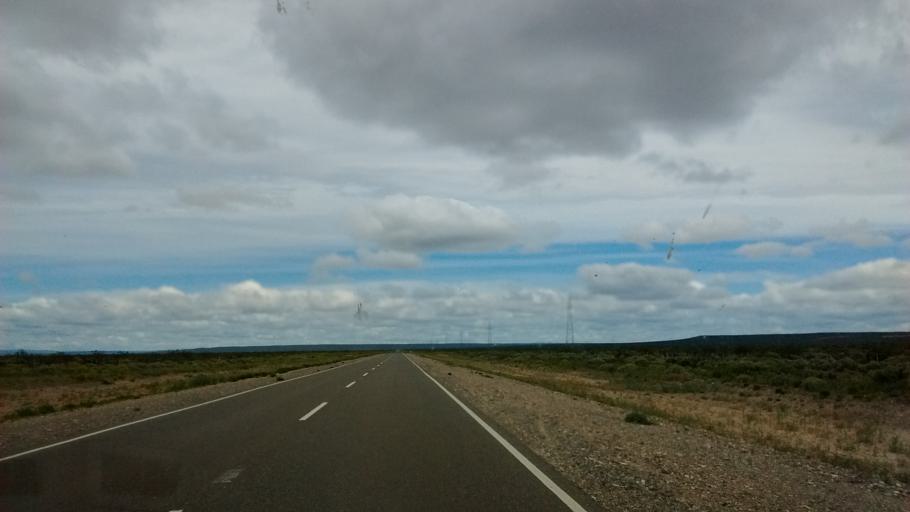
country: AR
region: Neuquen
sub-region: Departamento de Picun Leufu
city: Picun Leufu
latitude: -39.6665
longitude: -69.4363
